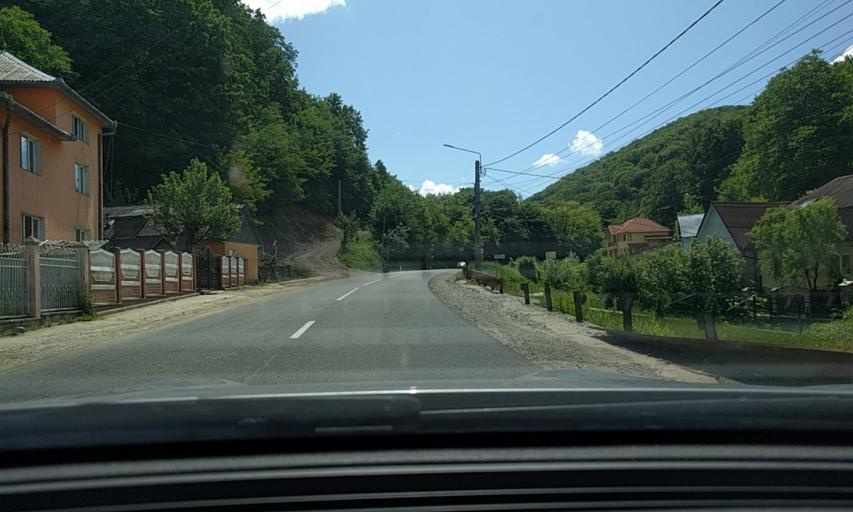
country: RO
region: Bistrita-Nasaud
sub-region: Oras Nasaud
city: Nasaud
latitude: 47.2781
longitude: 24.4219
